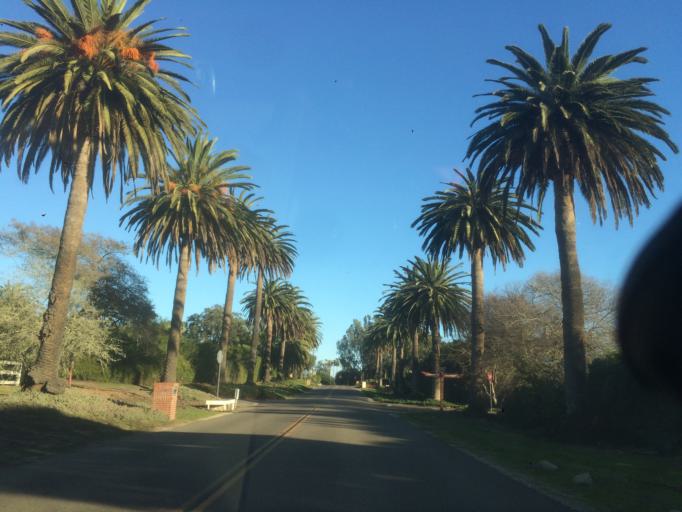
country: US
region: California
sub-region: Santa Barbara County
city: Santa Barbara
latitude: 34.4096
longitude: -119.7581
